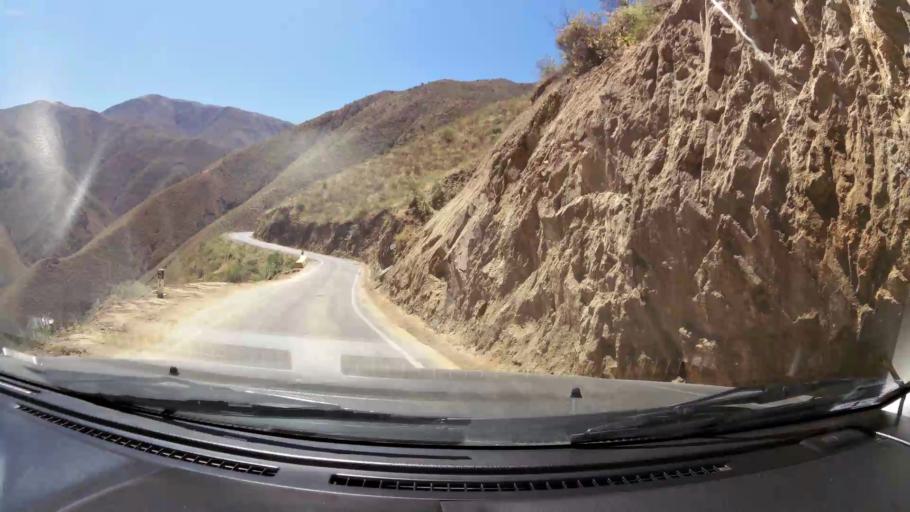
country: PE
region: Ica
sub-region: Provincia de Pisco
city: Huancano
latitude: -13.7229
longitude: -75.4542
